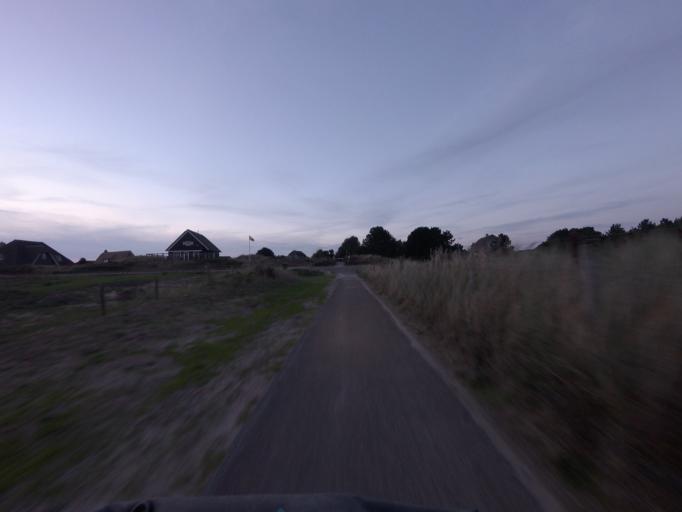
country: NL
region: Friesland
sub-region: Gemeente Ameland
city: Nes
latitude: 53.4552
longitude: 5.7960
